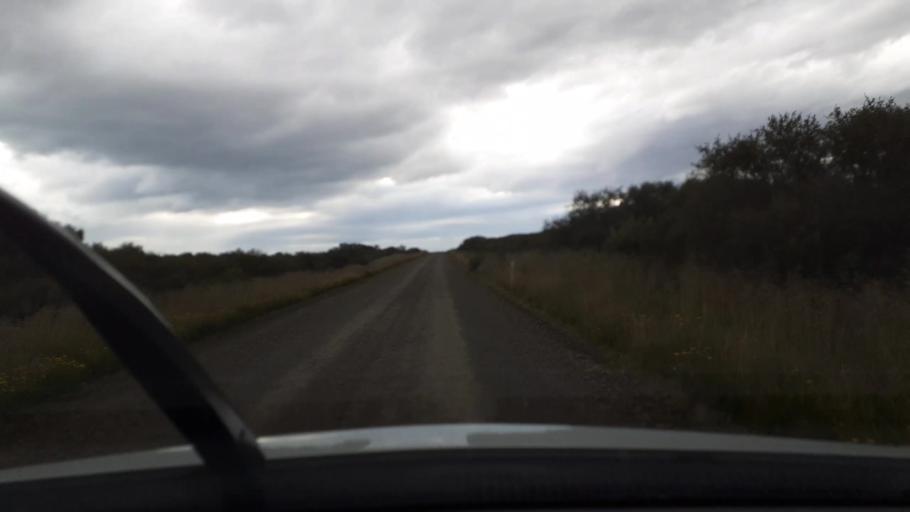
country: IS
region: West
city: Borgarnes
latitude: 64.6069
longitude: -21.9643
